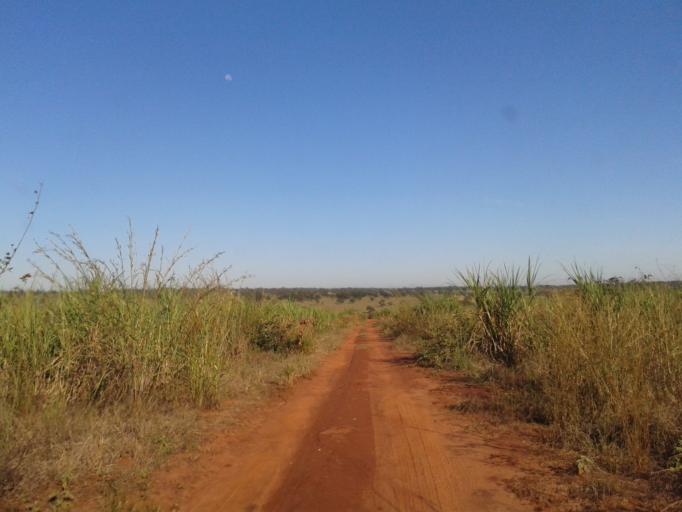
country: BR
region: Minas Gerais
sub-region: Santa Vitoria
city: Santa Vitoria
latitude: -19.0193
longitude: -50.3725
